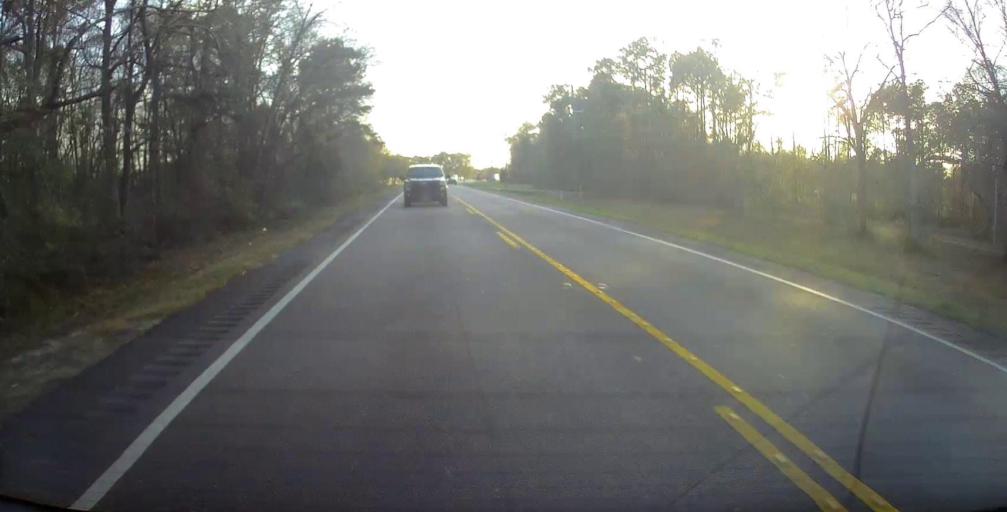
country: US
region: Georgia
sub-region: Effingham County
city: Guyton
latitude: 32.1862
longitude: -81.4515
